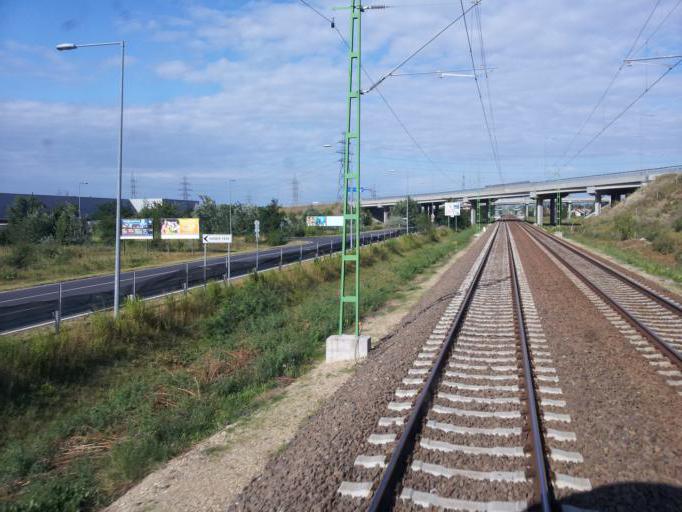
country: HU
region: Pest
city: Diosd
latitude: 47.3859
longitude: 18.9625
